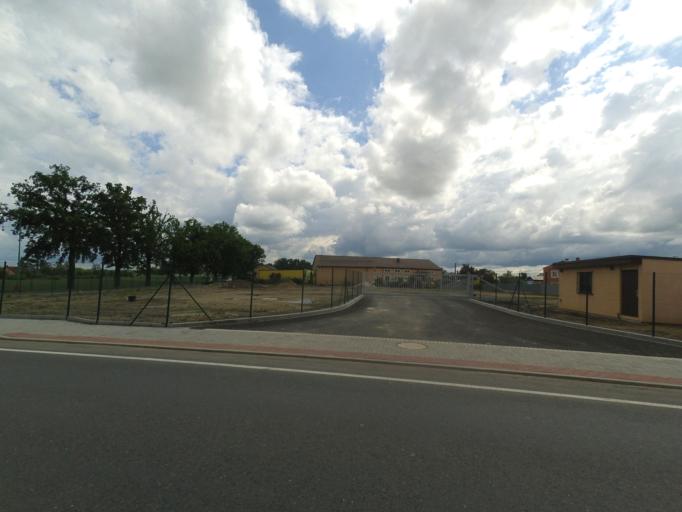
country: CZ
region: Plzensky
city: Bor
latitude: 49.7086
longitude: 12.7836
